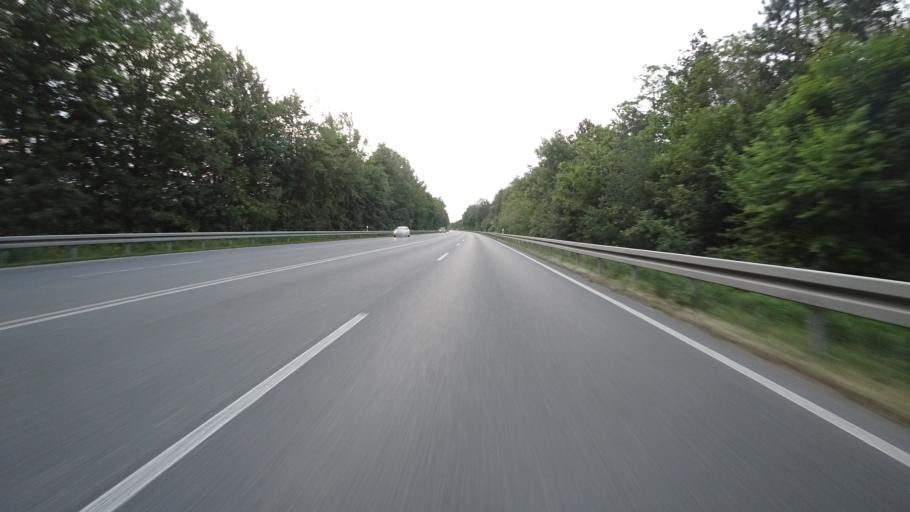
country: DE
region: North Rhine-Westphalia
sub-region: Regierungsbezirk Arnsberg
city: Lippstadt
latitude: 51.7061
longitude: 8.3593
